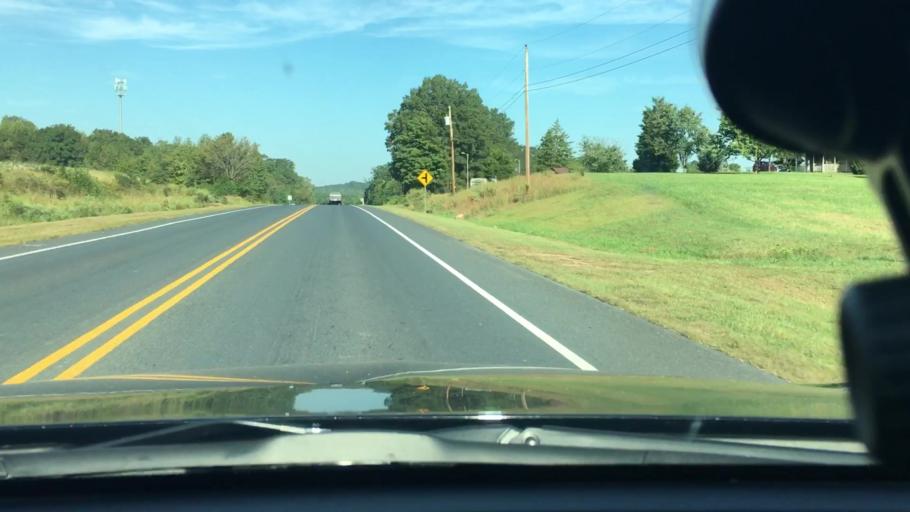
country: US
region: North Carolina
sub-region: Stanly County
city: Albemarle
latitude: 35.3798
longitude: -80.1739
